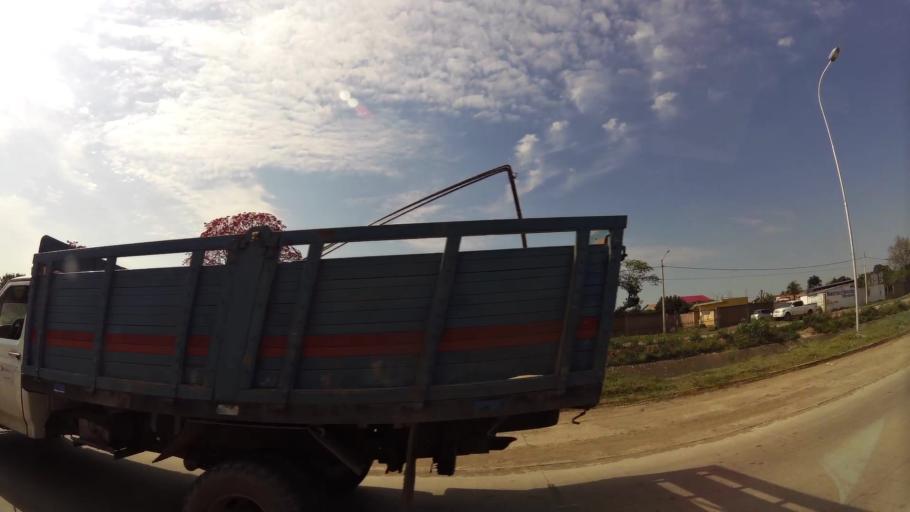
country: BO
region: Santa Cruz
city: Santa Cruz de la Sierra
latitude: -17.7243
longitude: -63.1460
